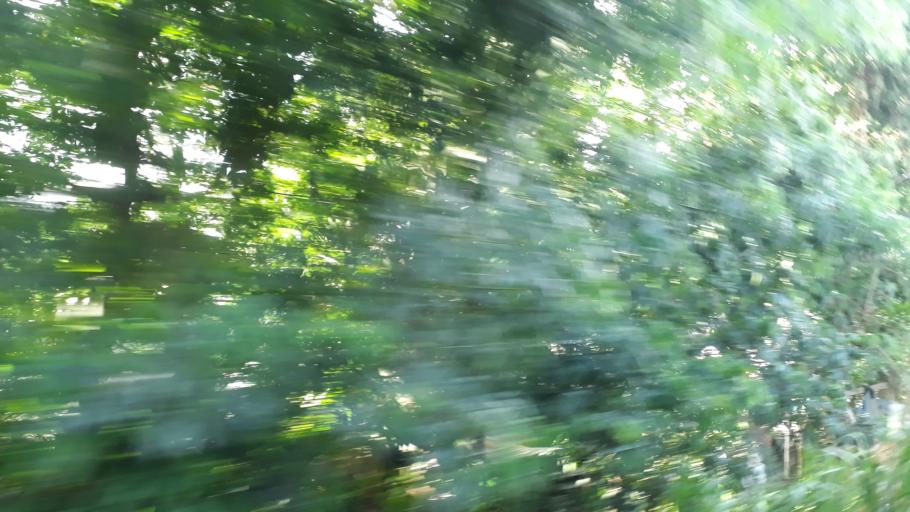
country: LK
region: Western
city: Kolonnawa
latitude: 6.9398
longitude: 79.8815
